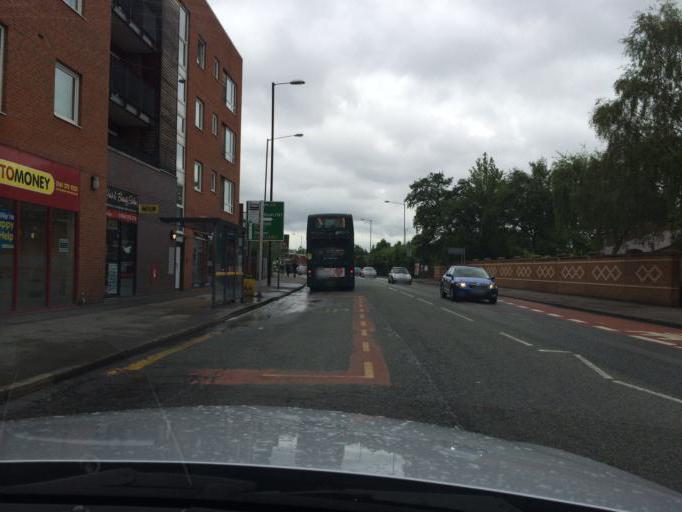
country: GB
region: England
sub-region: Manchester
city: Longsight
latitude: 53.4659
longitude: -2.2156
